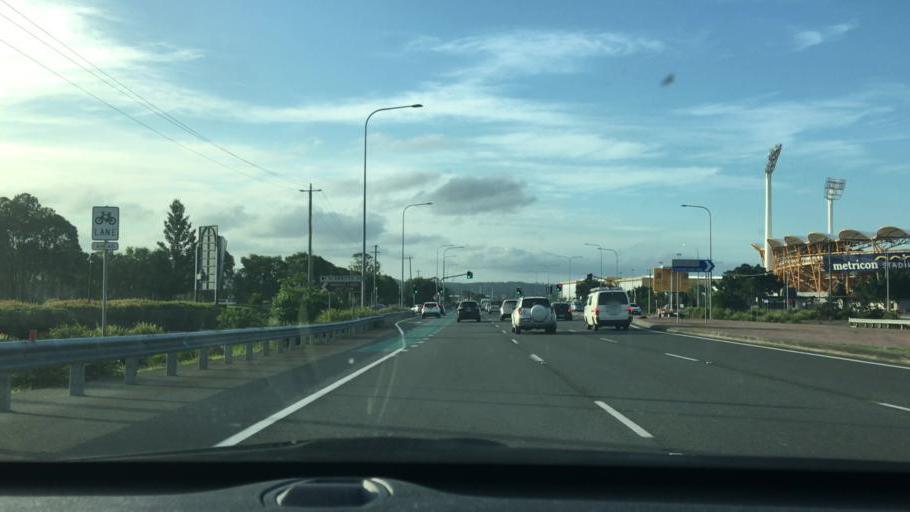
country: AU
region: Queensland
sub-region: Gold Coast
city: Nerang
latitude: -28.0101
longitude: 153.3676
